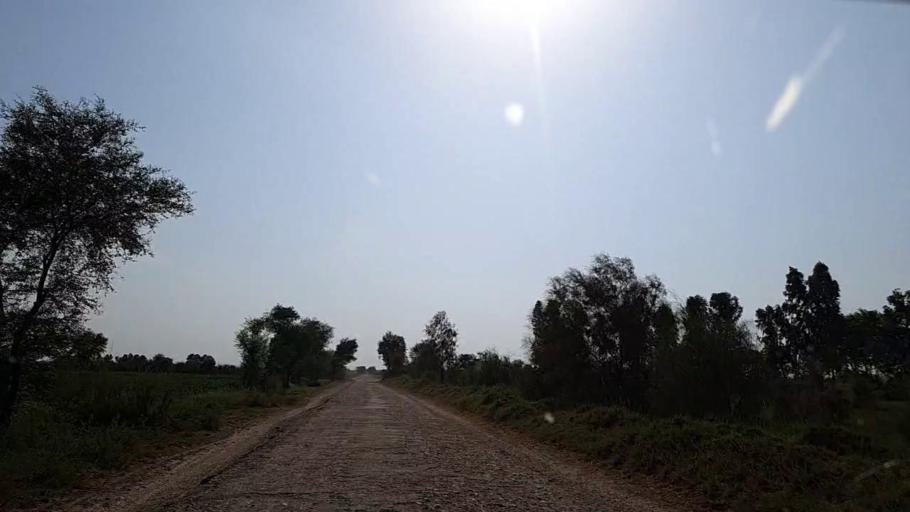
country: PK
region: Sindh
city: Khanpur
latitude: 27.7370
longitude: 69.3691
